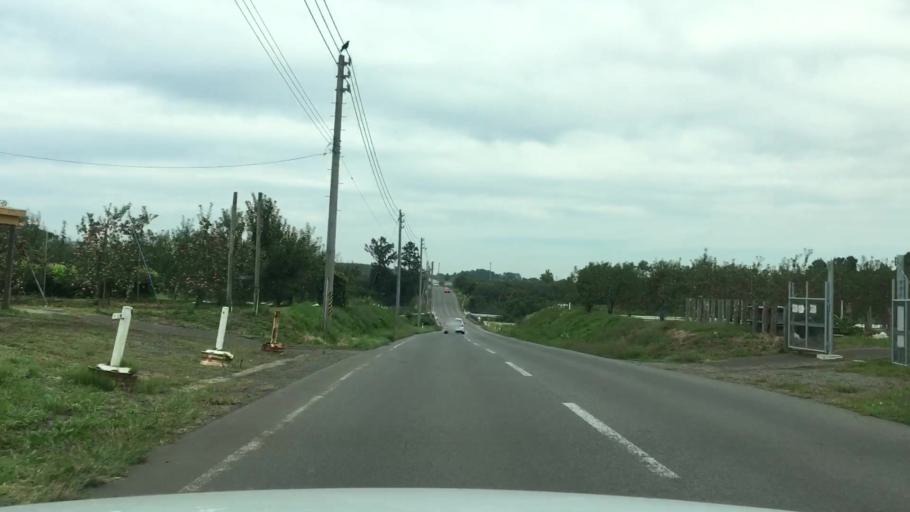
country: JP
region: Aomori
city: Hirosaki
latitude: 40.6543
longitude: 140.4210
